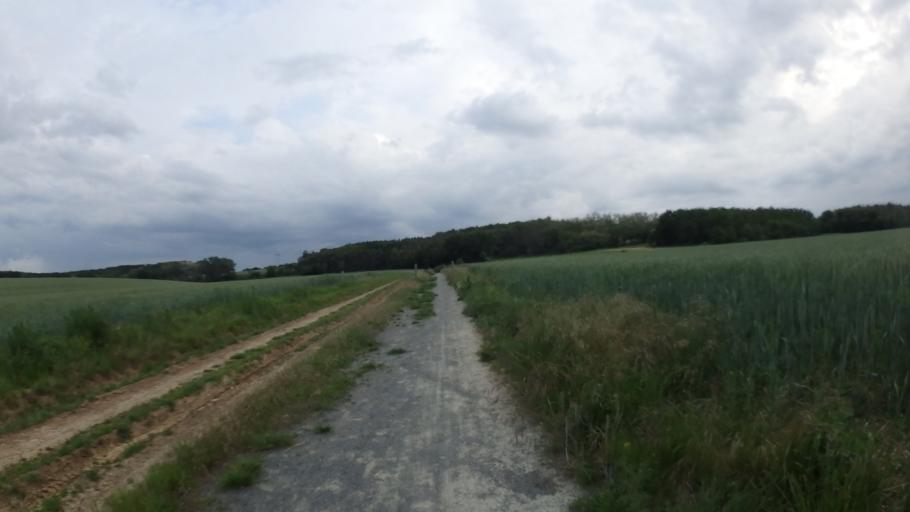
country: CZ
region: South Moravian
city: Moravany
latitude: 49.1388
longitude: 16.5701
